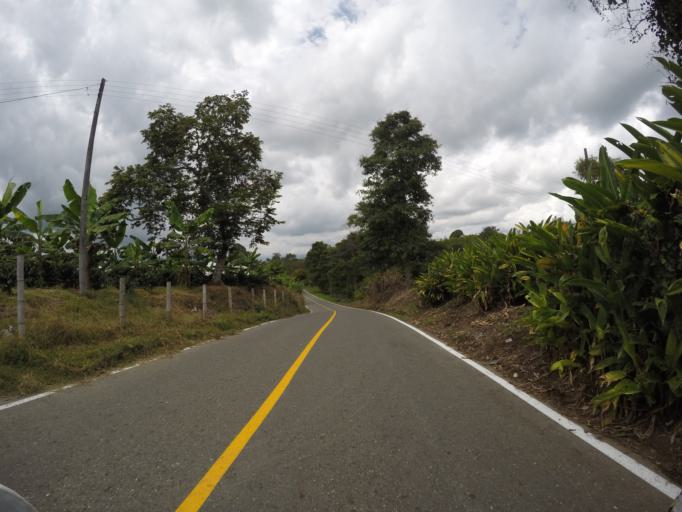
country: CO
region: Quindio
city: Quimbaya
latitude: 4.6093
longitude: -75.7400
